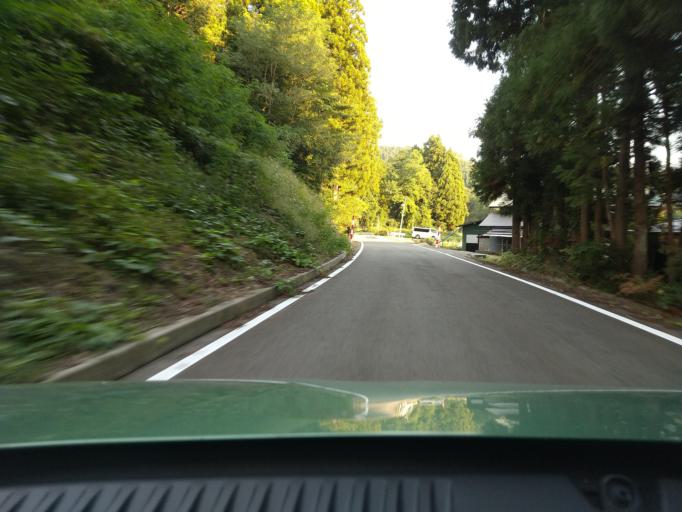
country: JP
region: Akita
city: Yokotemachi
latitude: 39.4181
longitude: 140.5882
